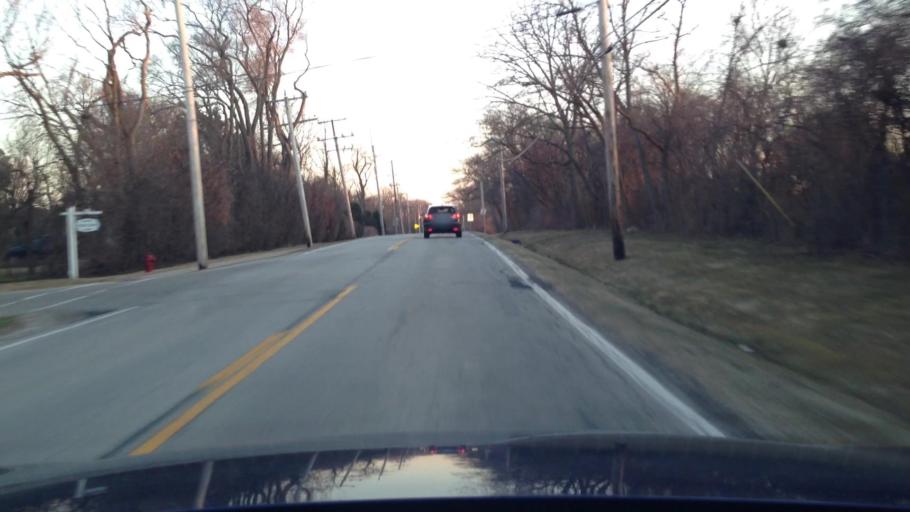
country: US
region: Illinois
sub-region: Cook County
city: Northfield
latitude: 42.1148
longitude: -87.7901
